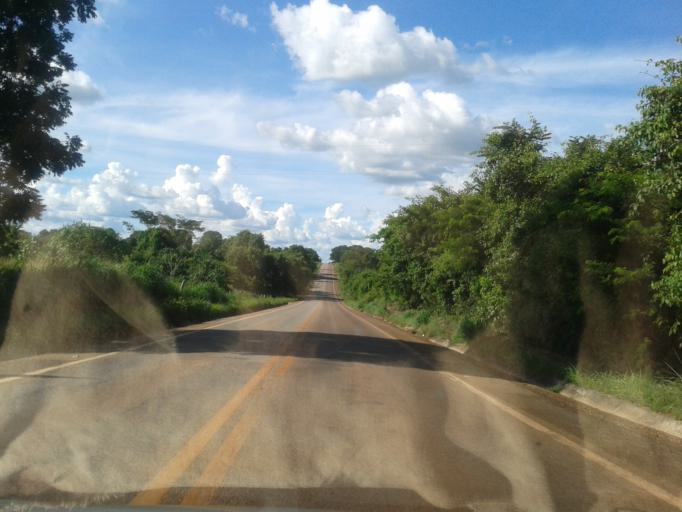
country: BR
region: Goias
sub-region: Mozarlandia
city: Mozarlandia
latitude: -14.7518
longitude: -50.5410
